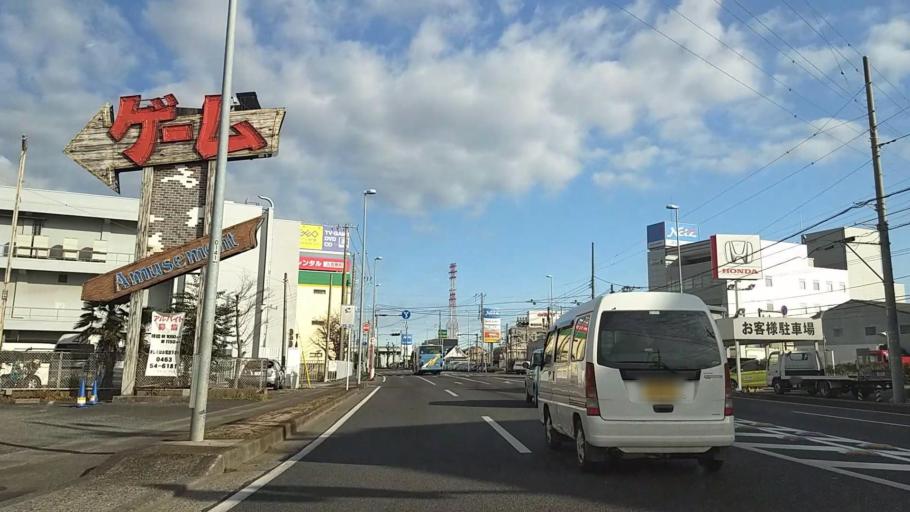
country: JP
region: Kanagawa
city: Hiratsuka
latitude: 35.3621
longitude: 139.3604
